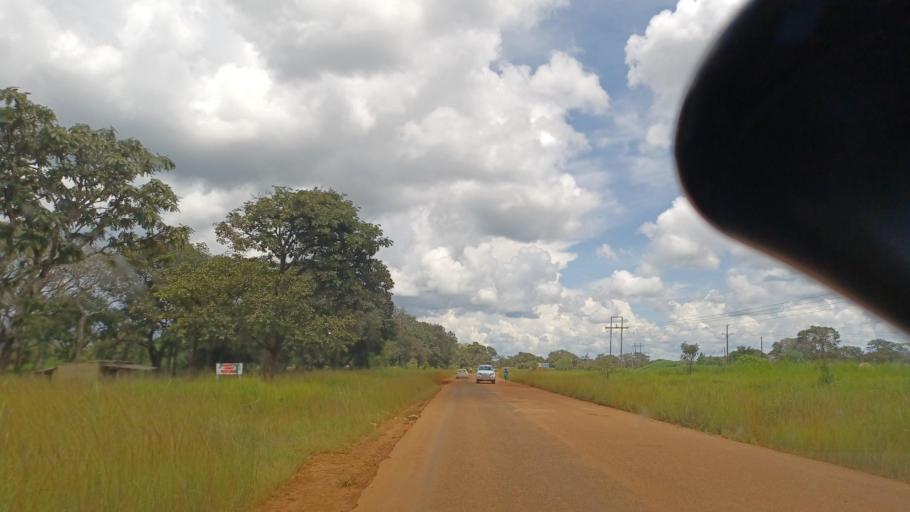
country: ZM
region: North-Western
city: Solwezi
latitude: -12.4799
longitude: 26.1982
